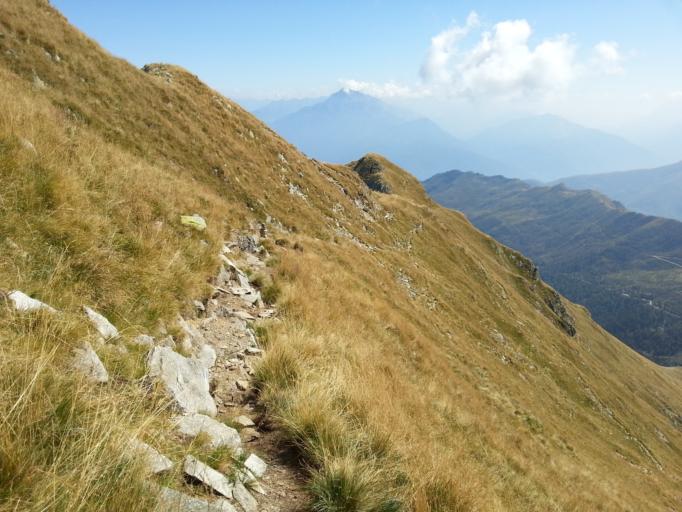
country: IT
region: Lombardy
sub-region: Provincia di Como
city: Garzeno
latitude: 46.1702
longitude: 9.1774
